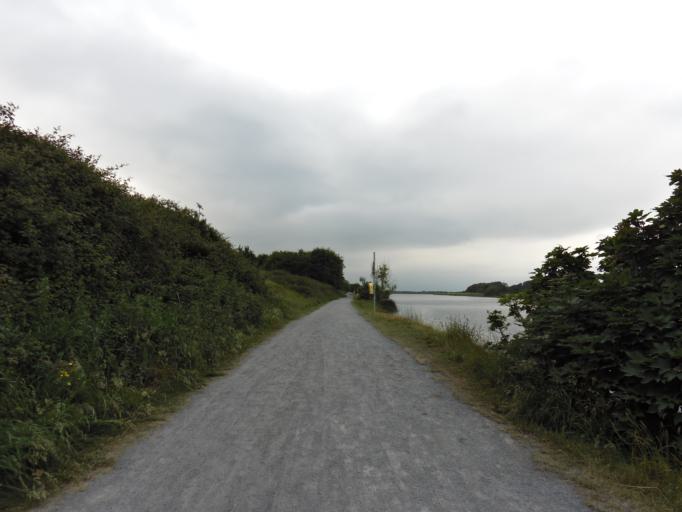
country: IE
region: Connaught
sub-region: County Galway
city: Gaillimh
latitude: 53.2947
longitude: -9.0730
